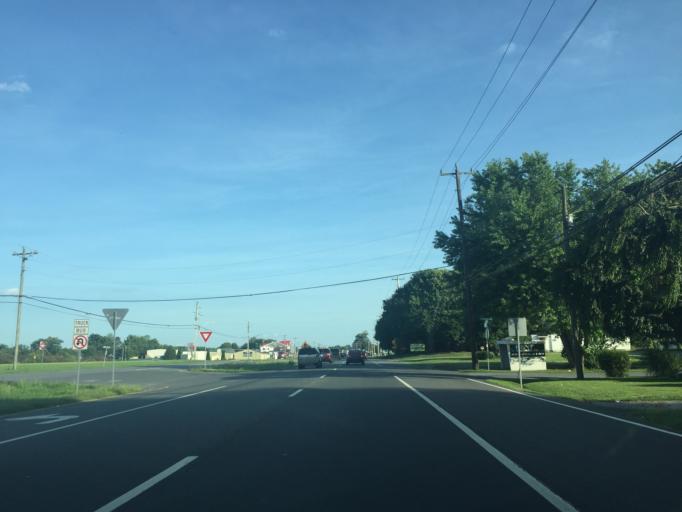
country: US
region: Delaware
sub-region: Kent County
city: Smyrna
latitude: 39.2732
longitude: -75.5903
